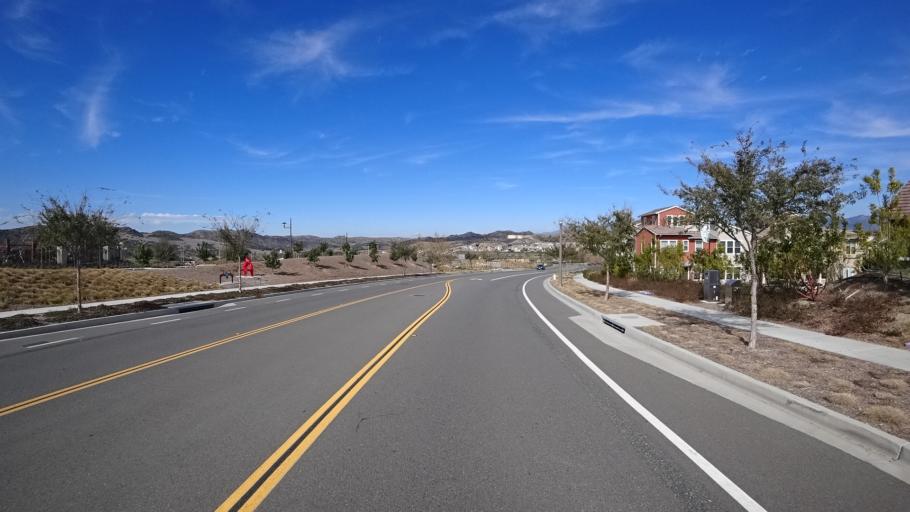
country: US
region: California
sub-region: Orange County
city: Ladera Ranch
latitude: 33.5462
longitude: -117.6007
